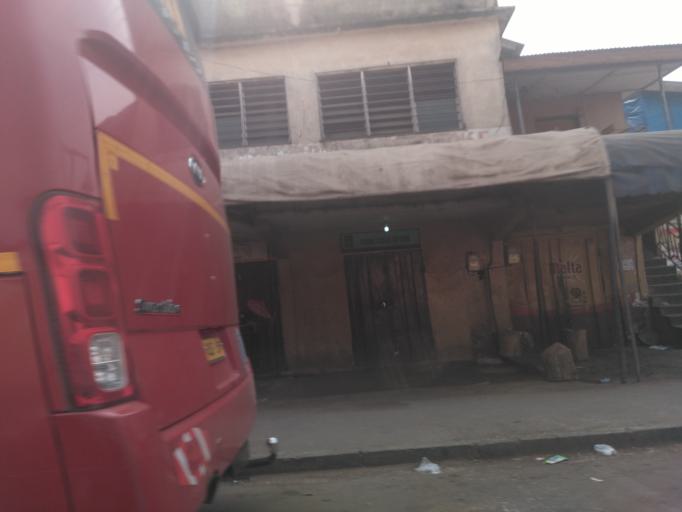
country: GH
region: Ashanti
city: Kumasi
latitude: 6.6883
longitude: -1.6164
